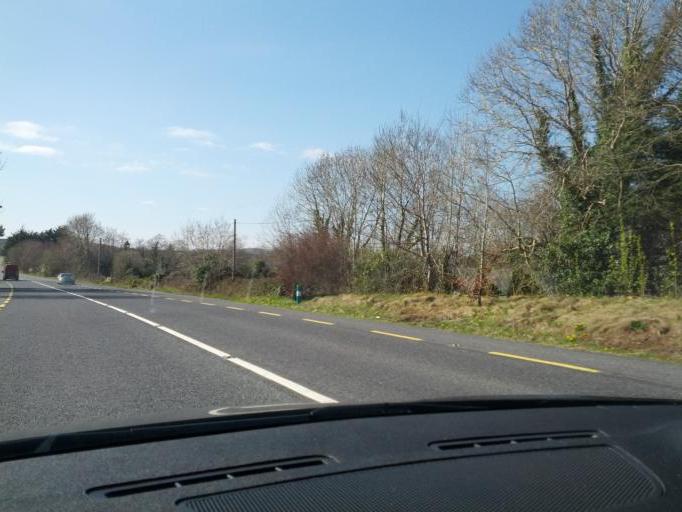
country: IE
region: Connaught
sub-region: County Galway
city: Moycullen
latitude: 53.3091
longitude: -9.1290
